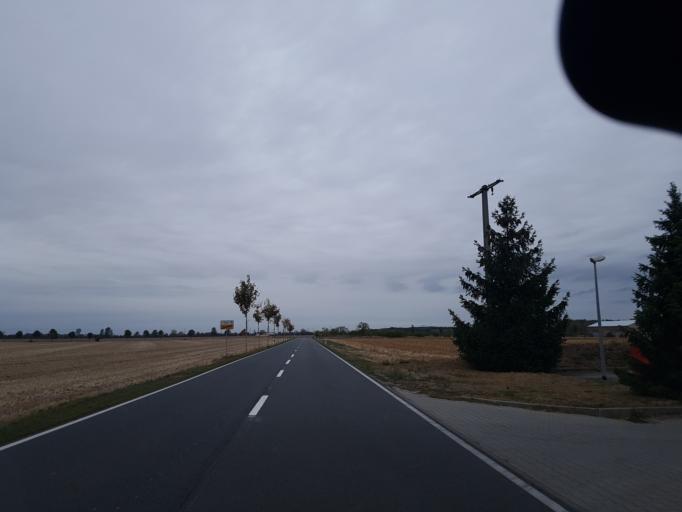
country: DE
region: Saxony-Anhalt
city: Prettin
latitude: 51.6693
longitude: 12.9162
